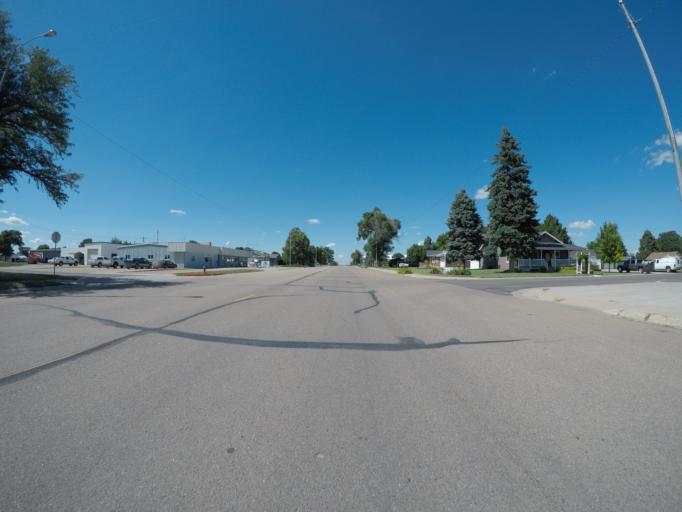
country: US
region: Nebraska
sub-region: Chase County
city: Imperial
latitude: 40.5253
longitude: -101.6431
